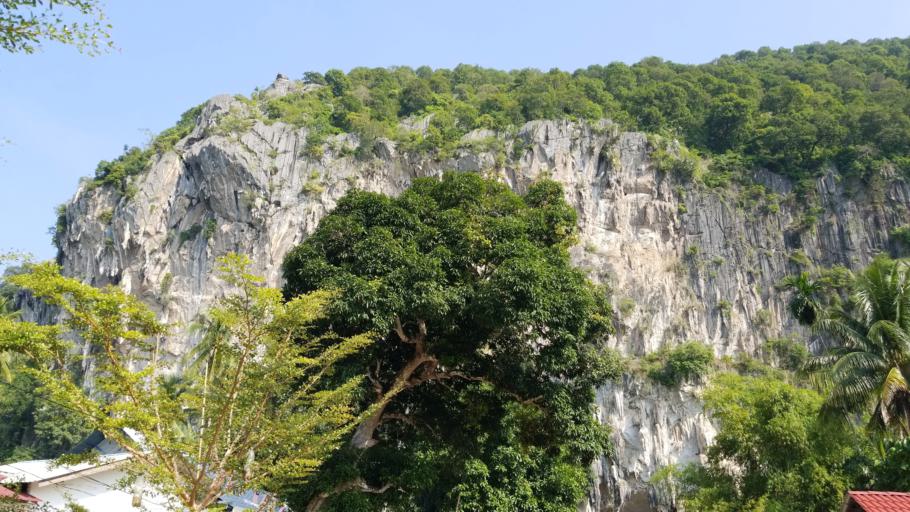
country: TH
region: Yala
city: Betong
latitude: 5.6708
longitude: 100.9099
